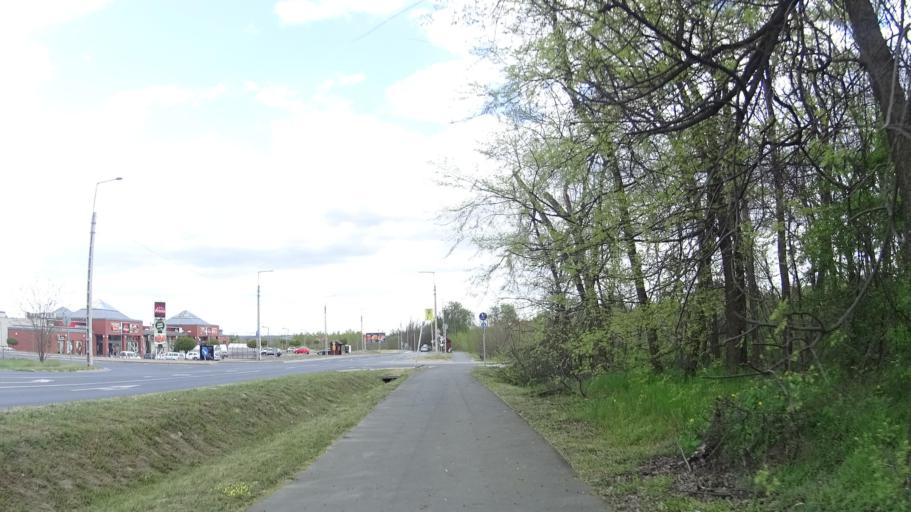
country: HU
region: Pest
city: Szada
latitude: 47.6241
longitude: 19.3236
